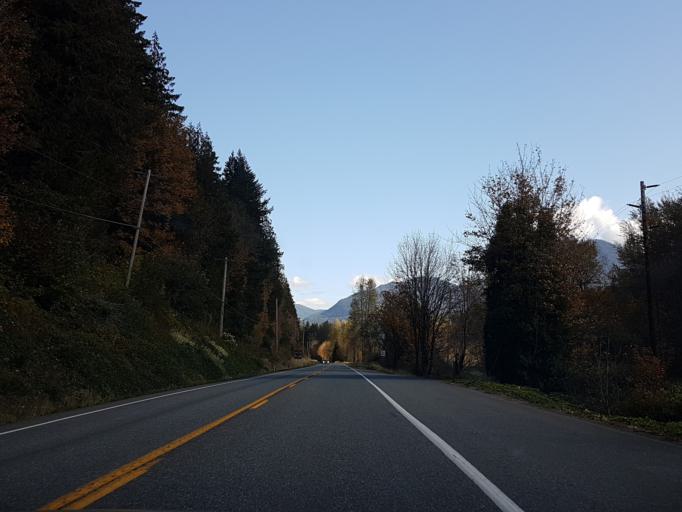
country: US
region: Washington
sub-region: Snohomish County
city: Gold Bar
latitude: 47.7352
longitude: -121.4240
